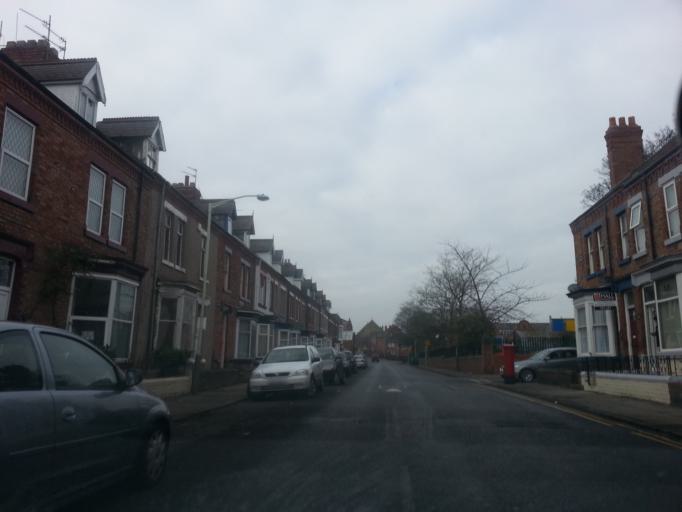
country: GB
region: England
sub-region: Darlington
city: Darlington
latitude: 54.5317
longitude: -1.5556
